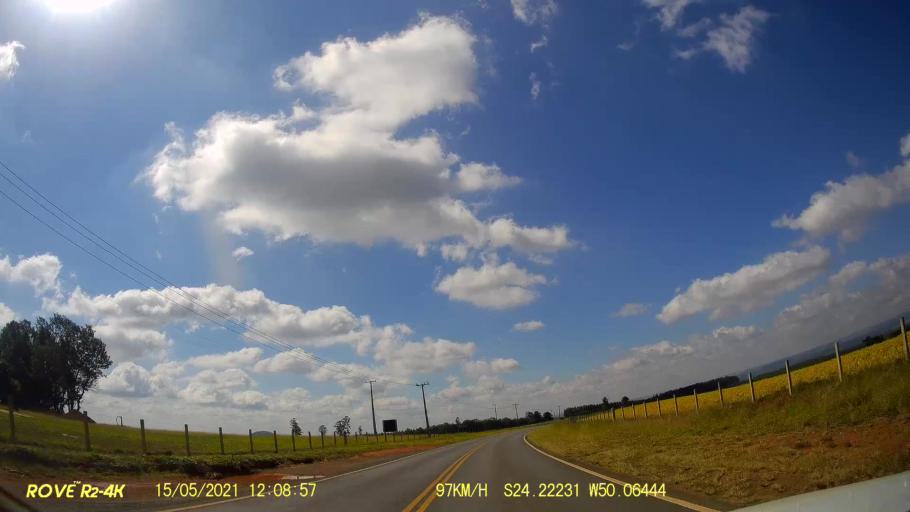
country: BR
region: Parana
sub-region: Pirai Do Sul
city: Pirai do Sul
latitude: -24.2225
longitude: -50.0647
